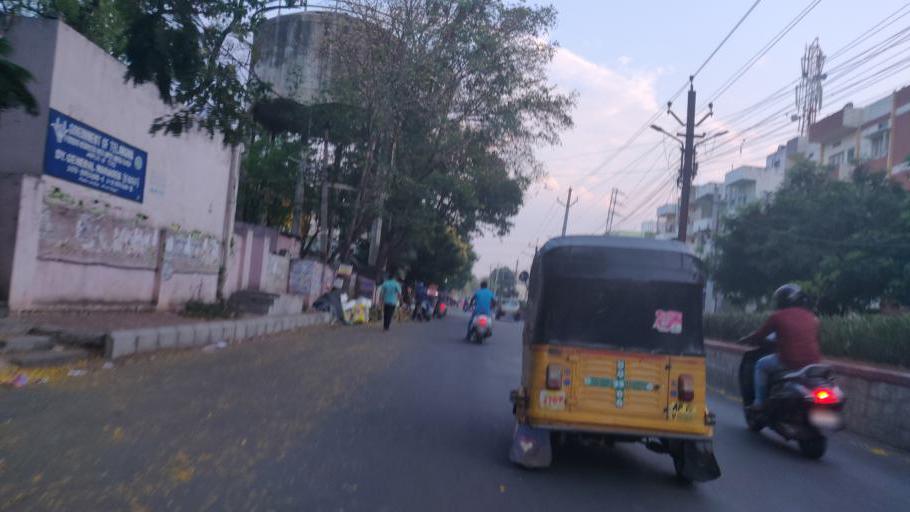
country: IN
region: Telangana
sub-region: Rangareddi
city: Gaddi Annaram
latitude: 17.3636
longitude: 78.5396
